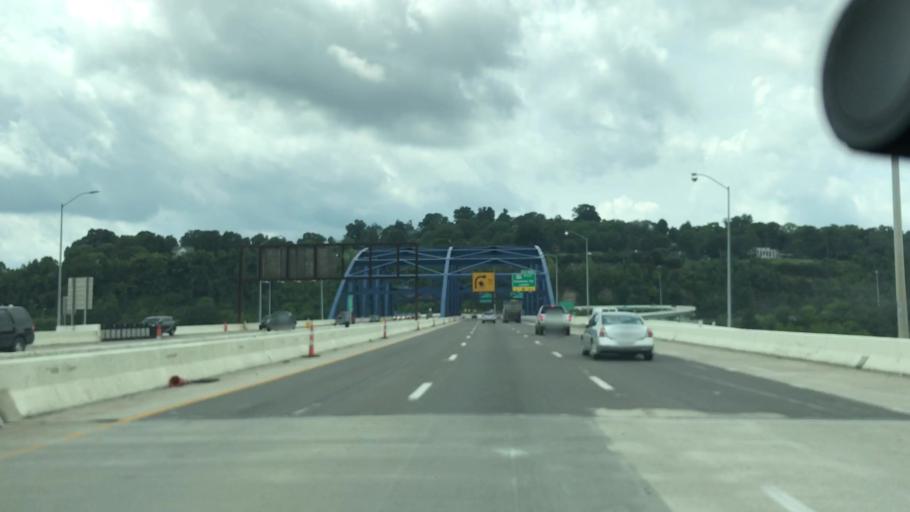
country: US
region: West Virginia
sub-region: Kanawha County
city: Charleston
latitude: 38.3564
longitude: -81.6466
